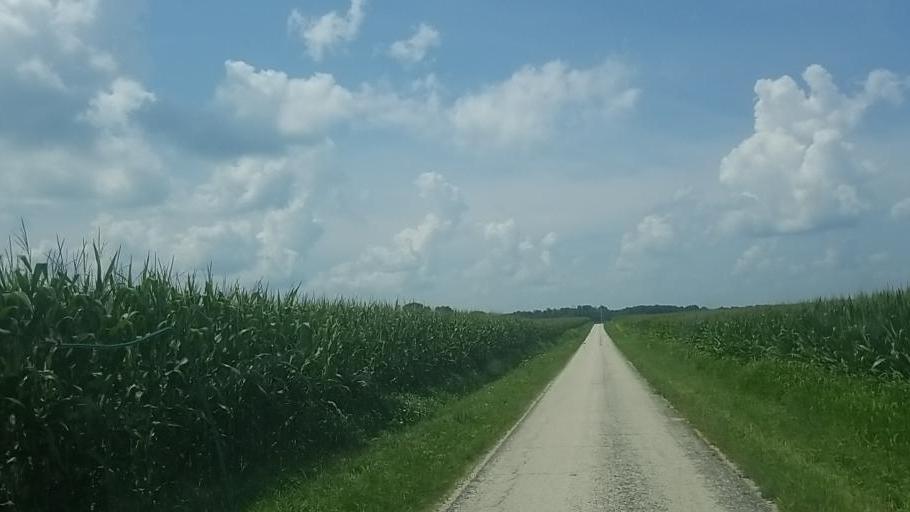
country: US
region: Ohio
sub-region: Crawford County
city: Bucyrus
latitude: 40.7460
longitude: -83.1076
